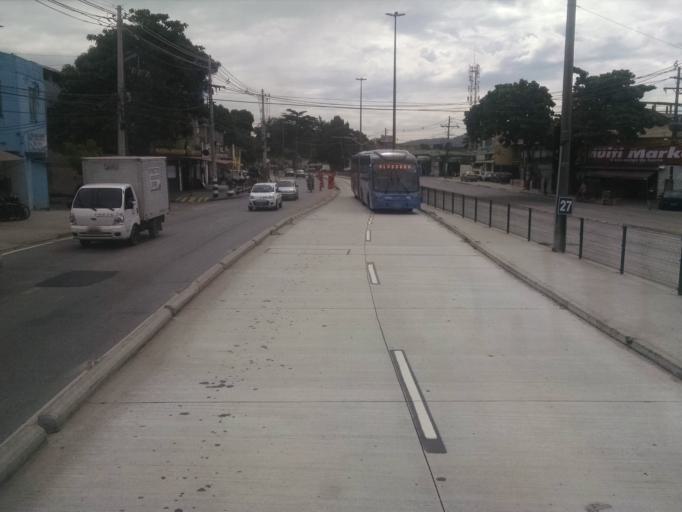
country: BR
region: Rio de Janeiro
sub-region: Sao Joao De Meriti
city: Sao Joao de Meriti
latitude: -22.9478
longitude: -43.3723
